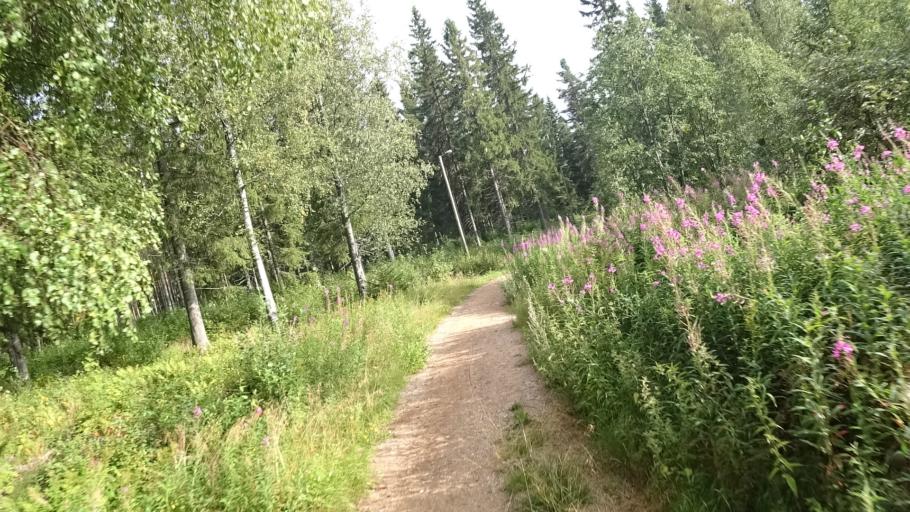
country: FI
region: North Karelia
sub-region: Joensuu
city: Ilomantsi
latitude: 62.6664
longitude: 30.9120
